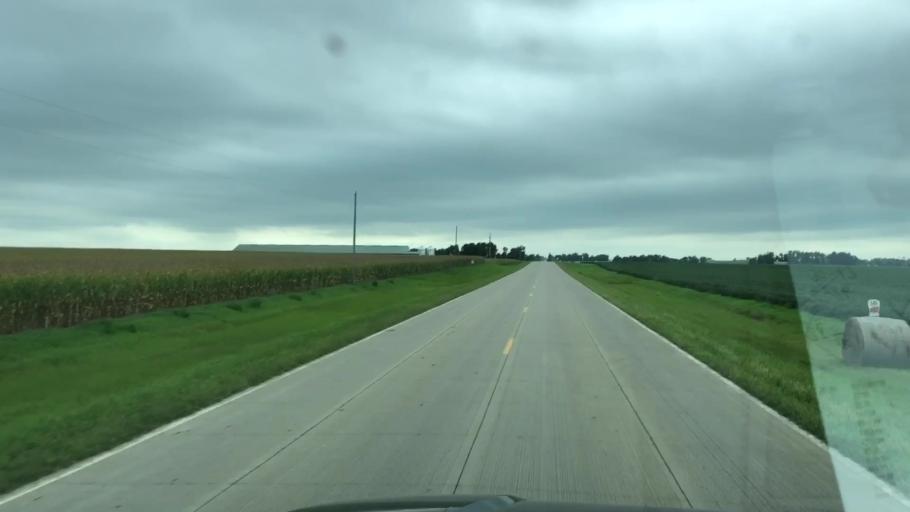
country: US
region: Iowa
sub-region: O'Brien County
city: Sheldon
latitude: 43.1265
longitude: -95.9790
